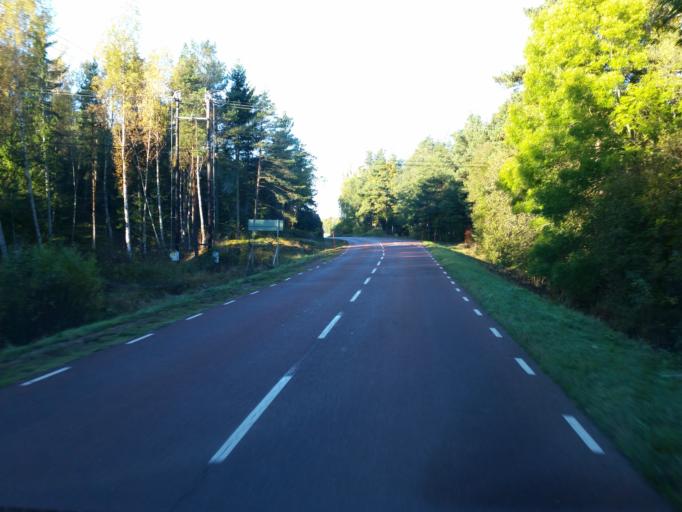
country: AX
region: Alands landsbygd
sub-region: Lumparland
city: Lumparland
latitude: 60.2060
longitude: 20.2824
